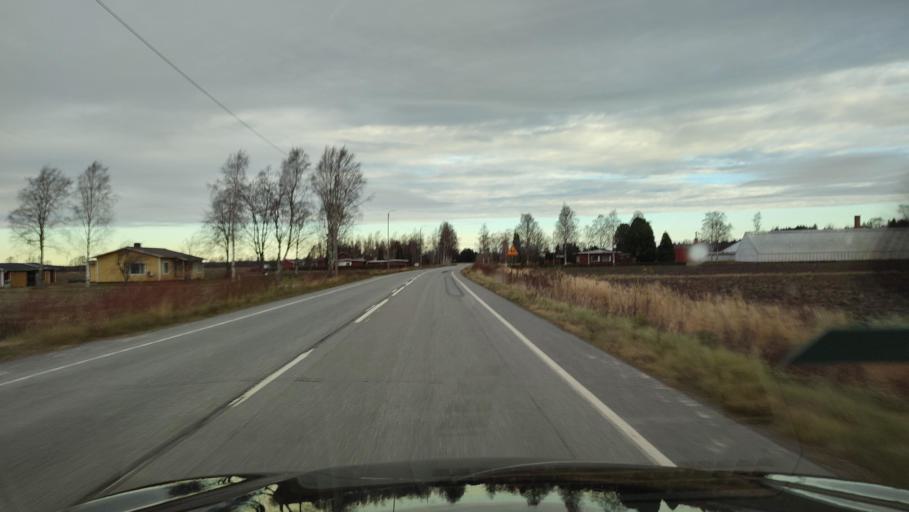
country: FI
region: Ostrobothnia
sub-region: Sydosterbotten
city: Naerpes
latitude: 62.4483
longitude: 21.3520
